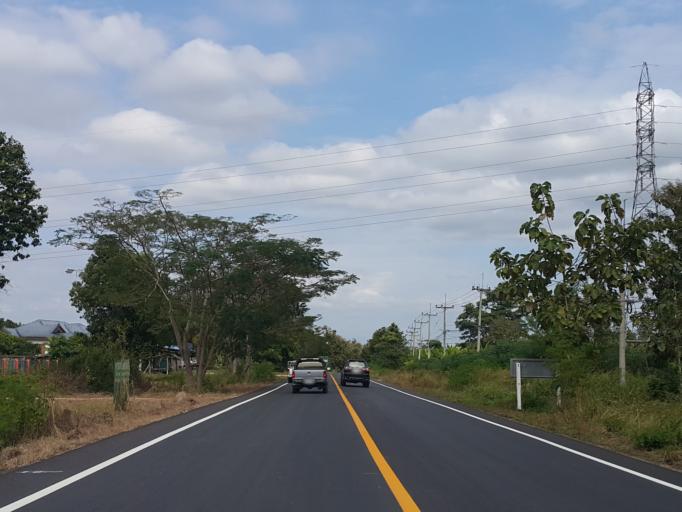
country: TH
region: Lampang
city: Lampang
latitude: 18.3677
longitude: 99.4561
